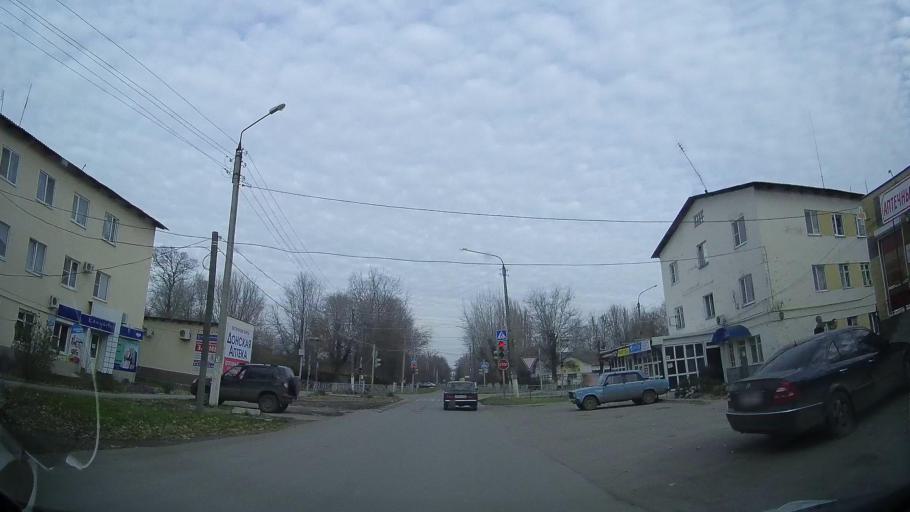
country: RU
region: Rostov
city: Zernograd
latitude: 46.8504
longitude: 40.3109
